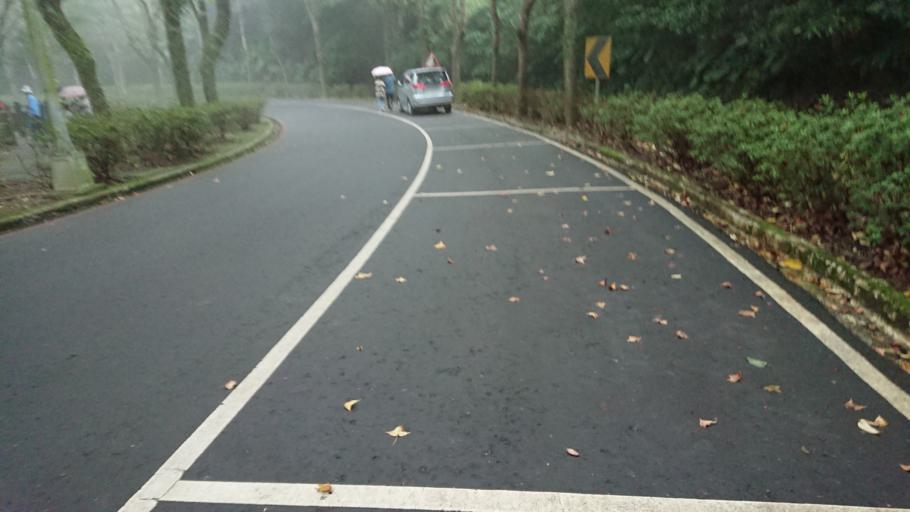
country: TW
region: Taiwan
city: Daxi
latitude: 24.8144
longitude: 121.2386
